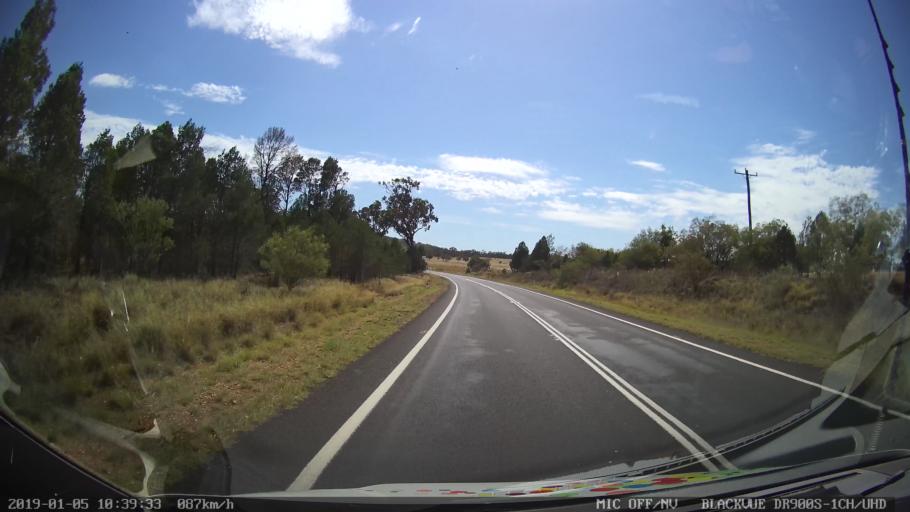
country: AU
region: New South Wales
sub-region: Gilgandra
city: Gilgandra
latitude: -31.4680
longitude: 148.9316
